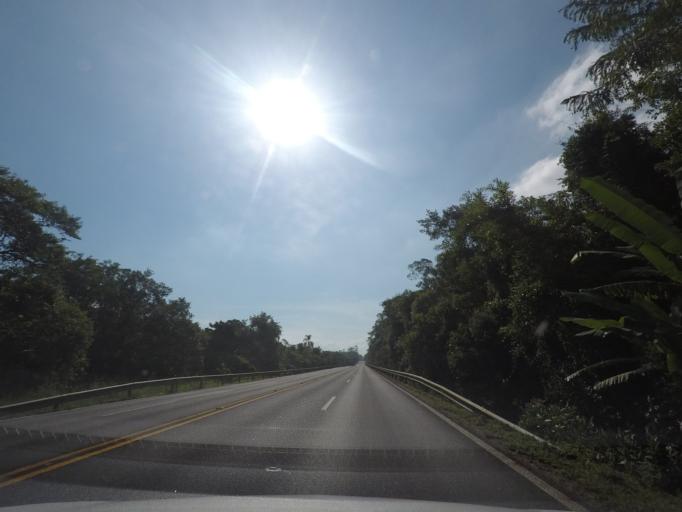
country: BR
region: Parana
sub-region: Pontal Do Parana
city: Pontal do Parana
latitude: -25.6154
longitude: -48.6026
